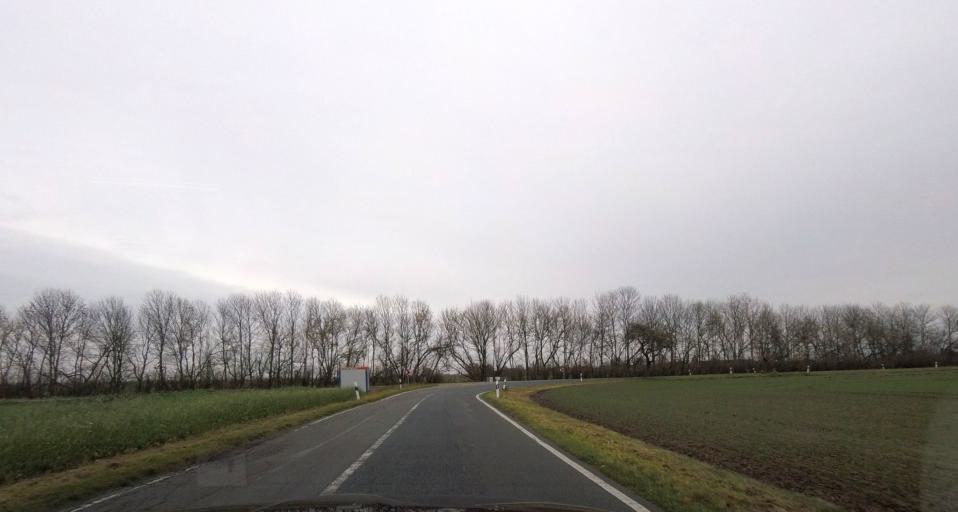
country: DE
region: Saxony-Anhalt
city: Zahna
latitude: 51.9800
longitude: 12.8222
